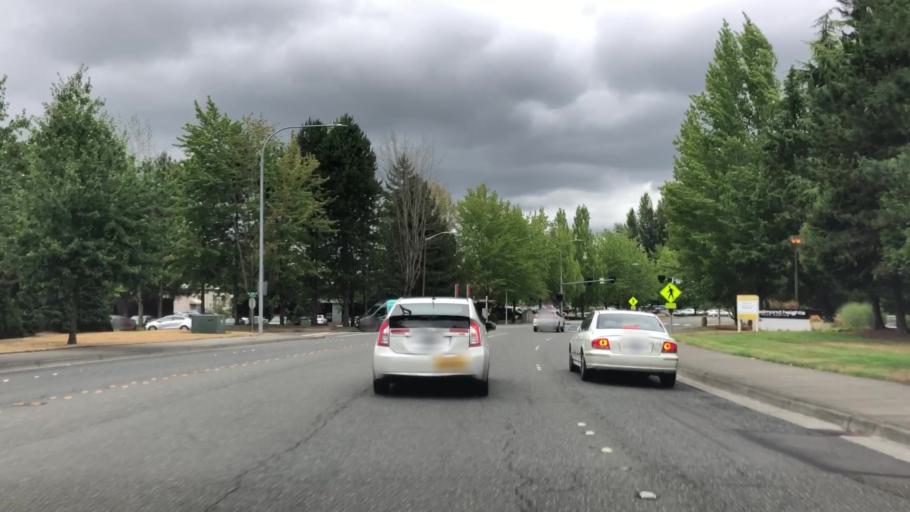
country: US
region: Washington
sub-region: King County
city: Redmond
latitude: 47.6800
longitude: -122.1455
